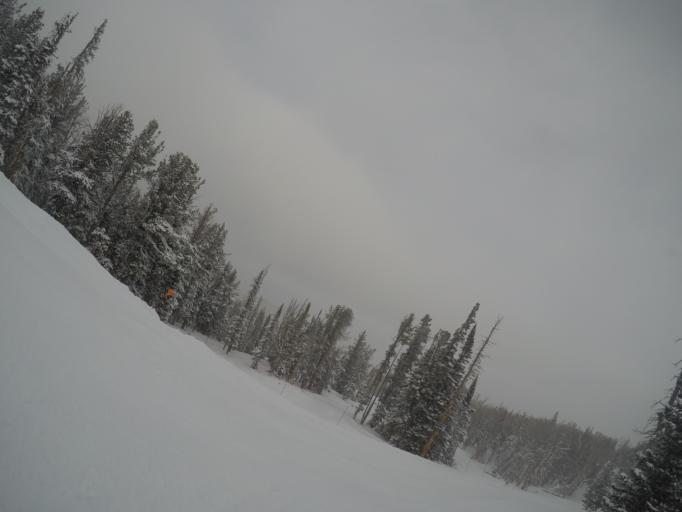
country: US
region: Montana
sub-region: Carbon County
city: Red Lodge
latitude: 45.1848
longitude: -109.3688
